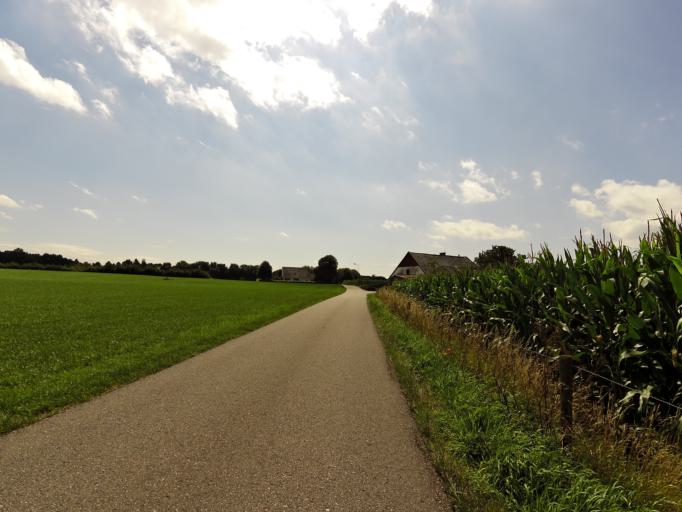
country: NL
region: Gelderland
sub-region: Gemeente Doesburg
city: Doesburg
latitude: 51.9525
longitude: 6.1350
